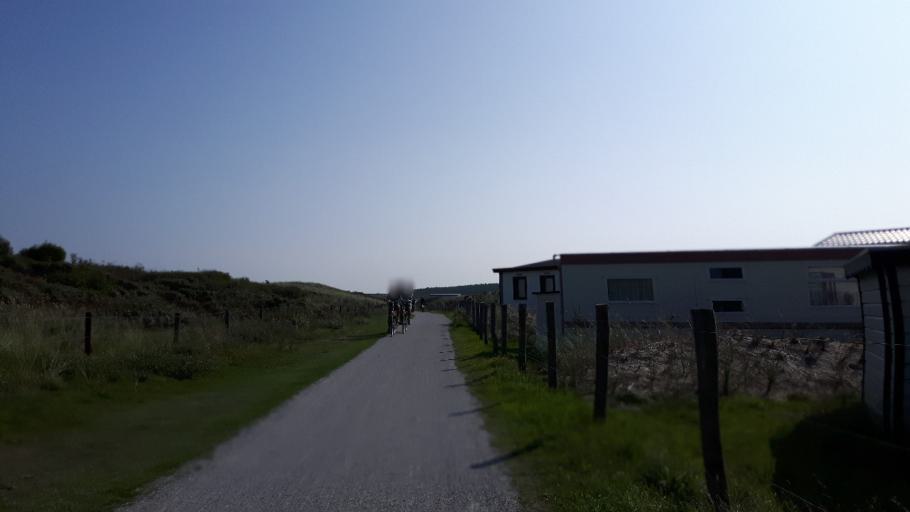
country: NL
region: Friesland
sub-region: Gemeente Ameland
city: Nes
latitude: 53.4585
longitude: 5.7698
